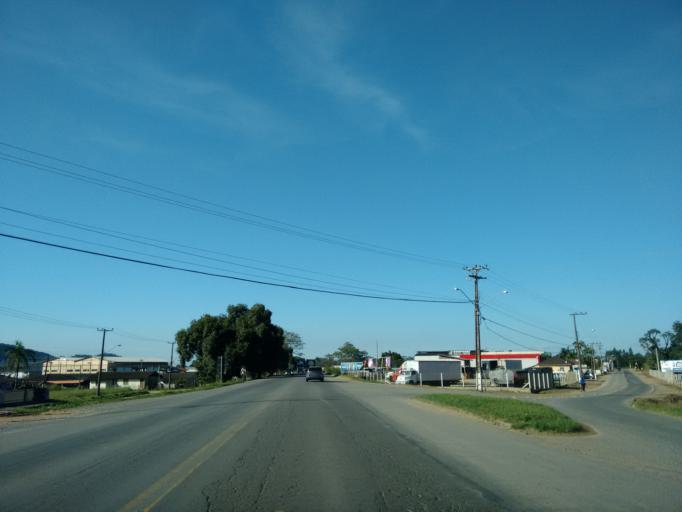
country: BR
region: Santa Catarina
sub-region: Guaramirim
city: Guaramirim
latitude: -26.4713
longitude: -48.9713
